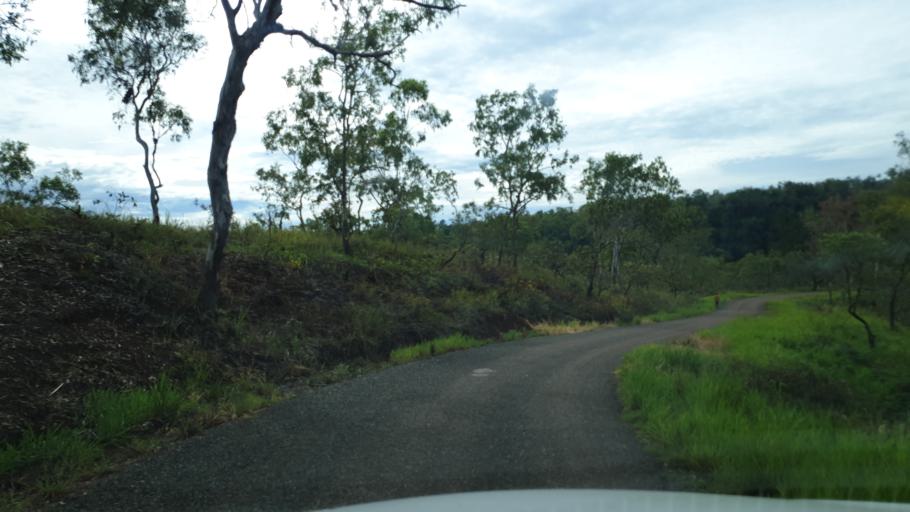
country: PG
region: National Capital
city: Port Moresby
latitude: -9.4329
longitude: 147.3960
